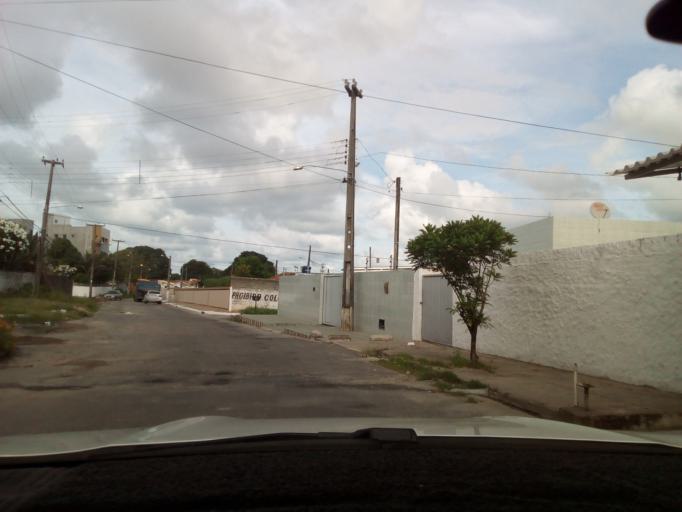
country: BR
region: Paraiba
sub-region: Joao Pessoa
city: Joao Pessoa
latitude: -7.1688
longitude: -34.8514
